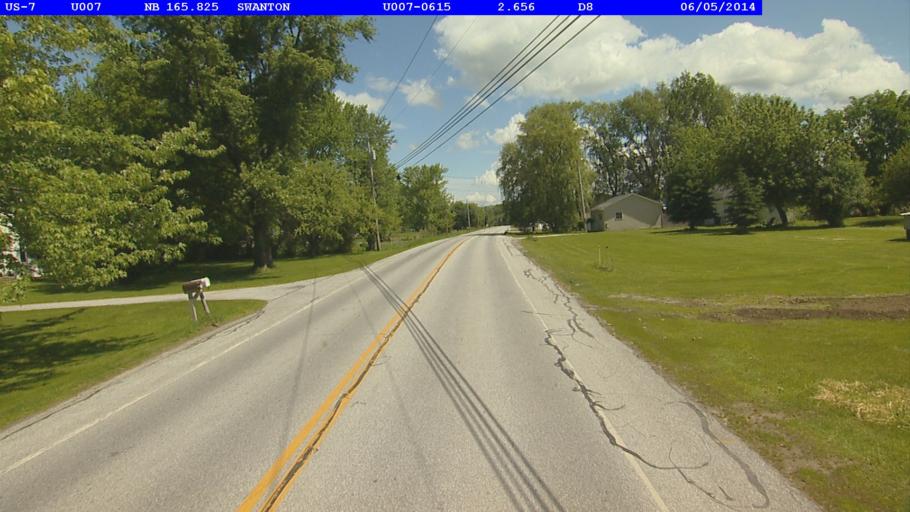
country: US
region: Vermont
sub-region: Franklin County
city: Swanton
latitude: 44.8850
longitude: -73.0933
